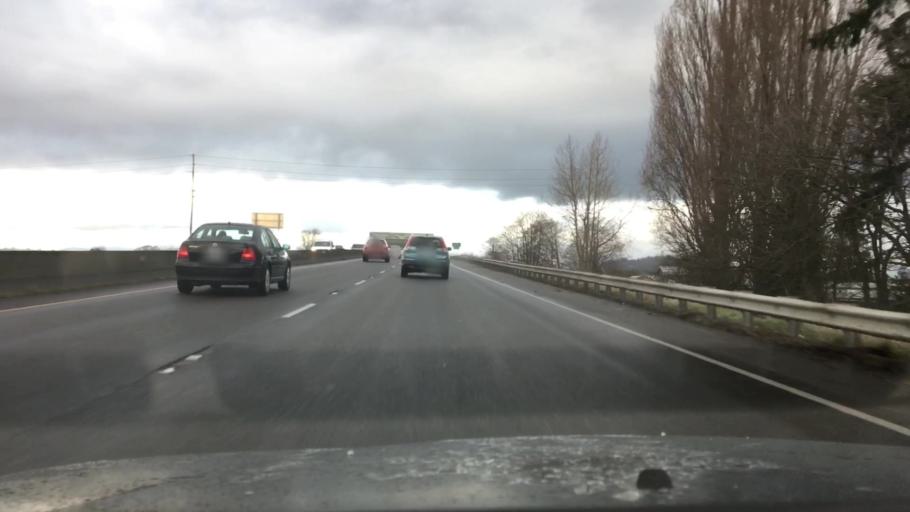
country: US
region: Washington
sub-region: Skagit County
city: Mount Vernon
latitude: 48.4417
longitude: -122.3409
